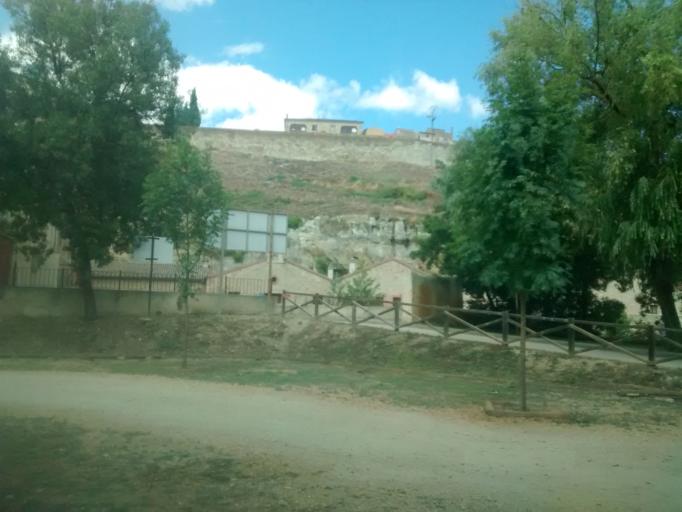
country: ES
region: Castille and Leon
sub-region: Provincia de Salamanca
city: Ciudad Rodrigo
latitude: 40.5944
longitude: -6.5339
